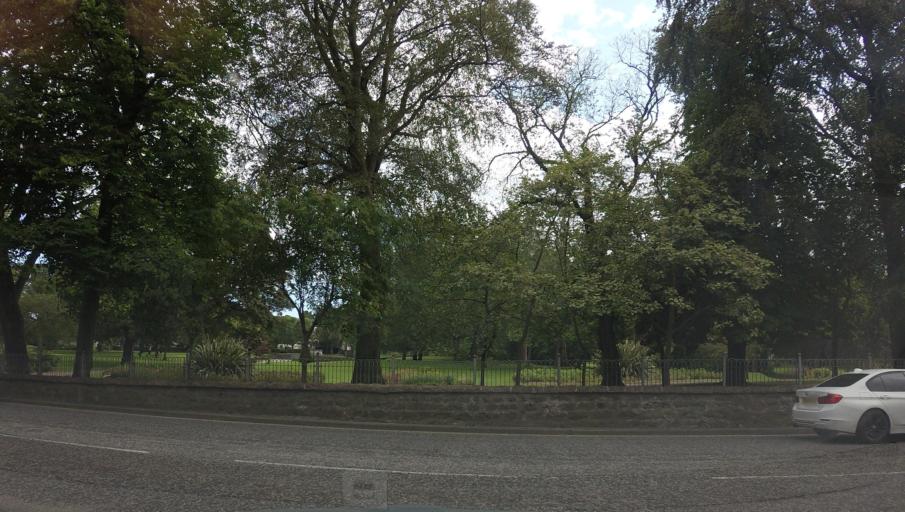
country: GB
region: Scotland
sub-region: Aberdeen City
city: Aberdeen
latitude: 57.1528
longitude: -2.1231
